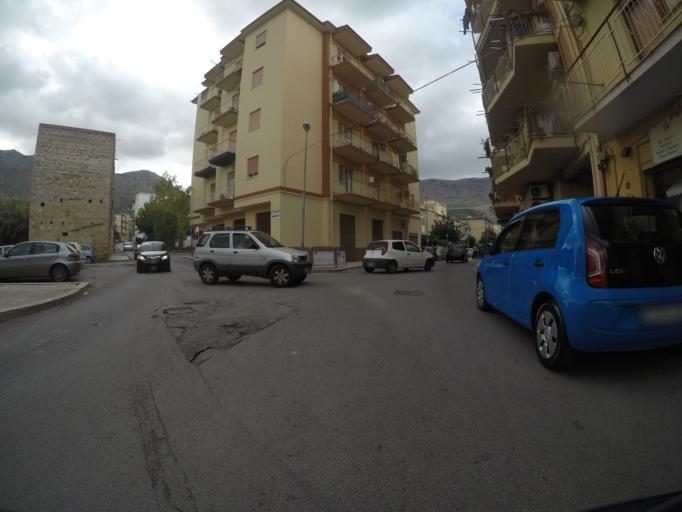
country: IT
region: Sicily
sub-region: Palermo
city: Carini
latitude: 38.1364
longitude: 13.1875
